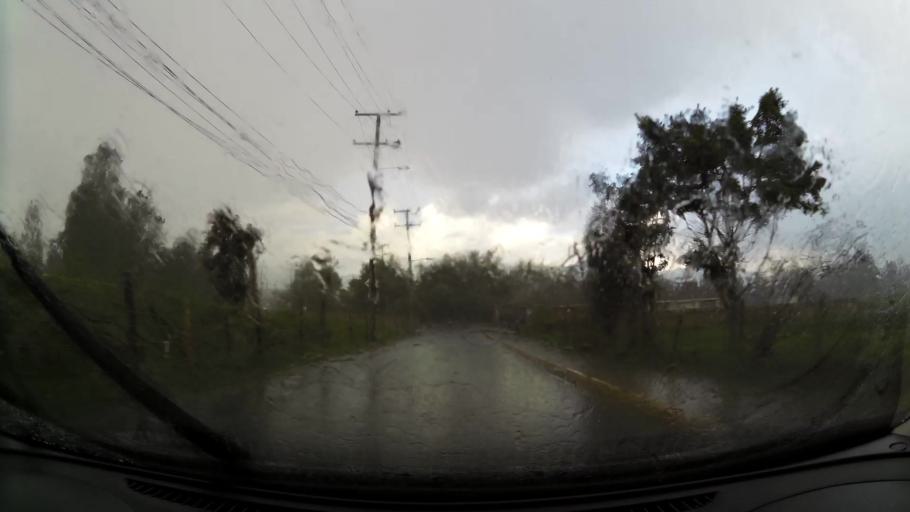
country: CO
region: Cundinamarca
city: Chia
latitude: 4.8625
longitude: -74.0680
